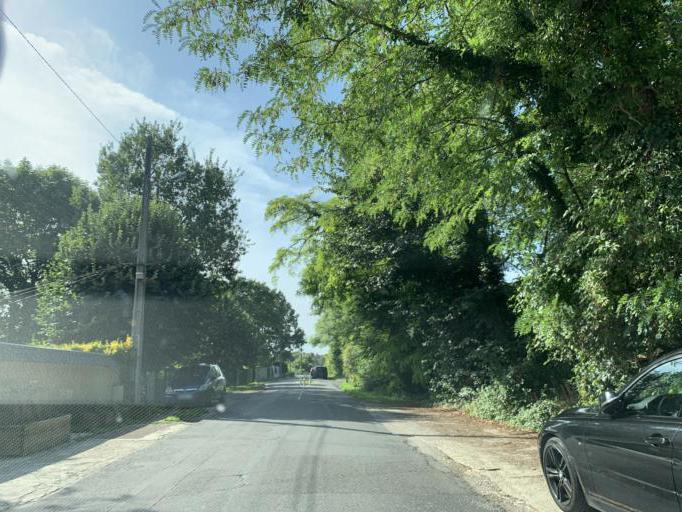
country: FR
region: Ile-de-France
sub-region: Departement de Seine-et-Marne
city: Chalifert
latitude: 48.9053
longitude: 2.7706
